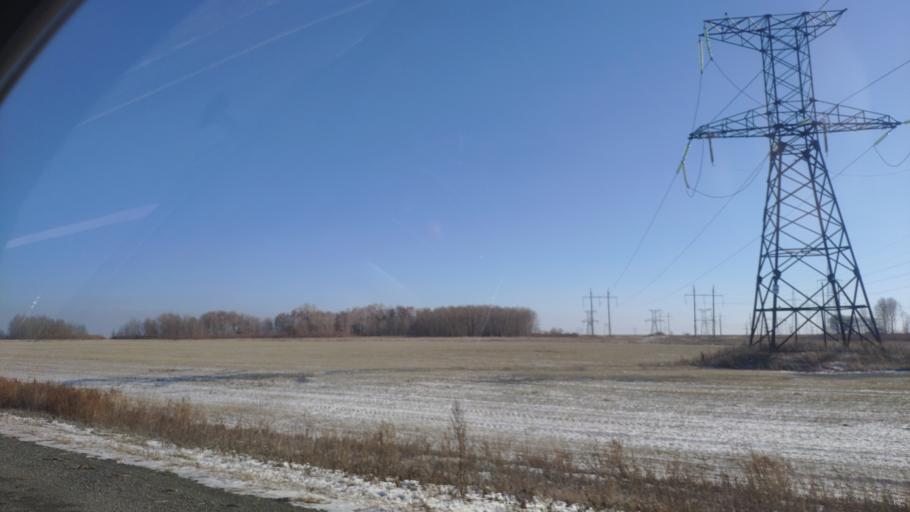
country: RU
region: Orenburg
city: Mednogorsk
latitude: 51.3229
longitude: 57.6037
